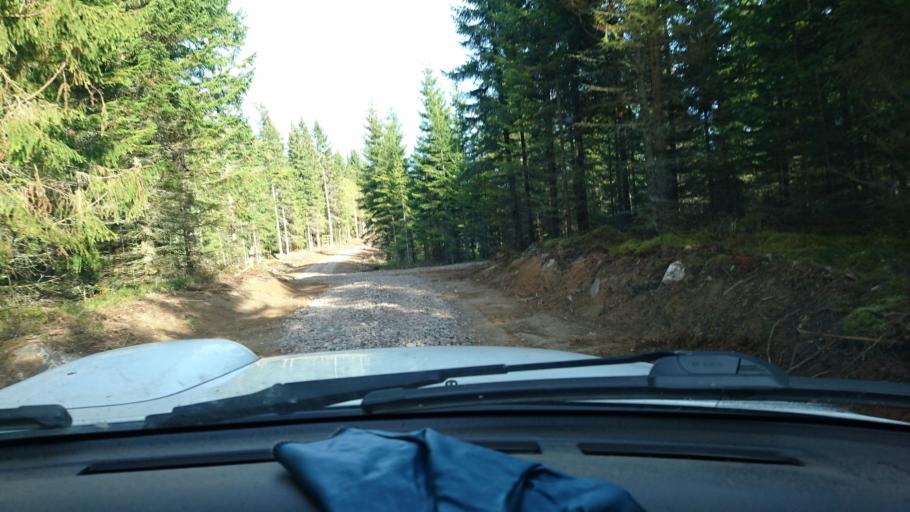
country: SE
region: Vaestra Goetaland
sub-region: Ulricehamns Kommun
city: Ulricehamn
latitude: 57.9402
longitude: 13.5515
